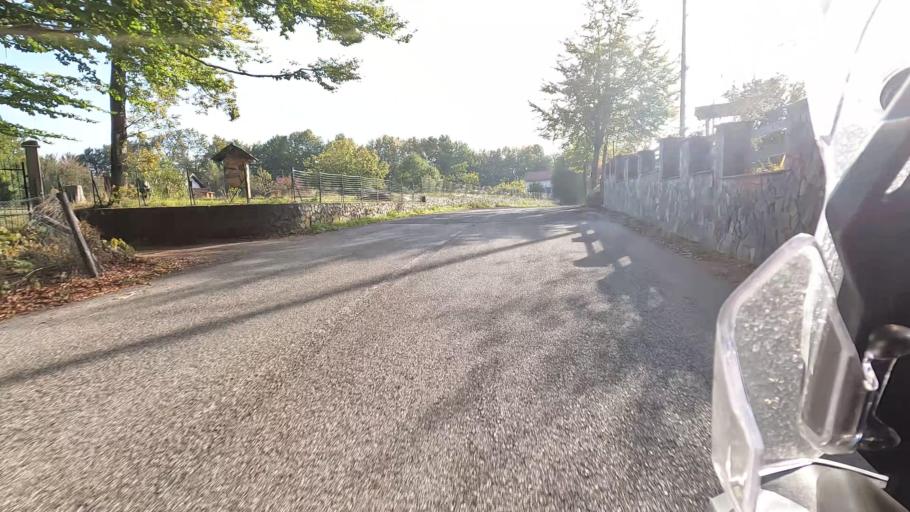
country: IT
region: Liguria
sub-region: Provincia di Savona
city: Urbe
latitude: 44.4694
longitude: 8.5605
